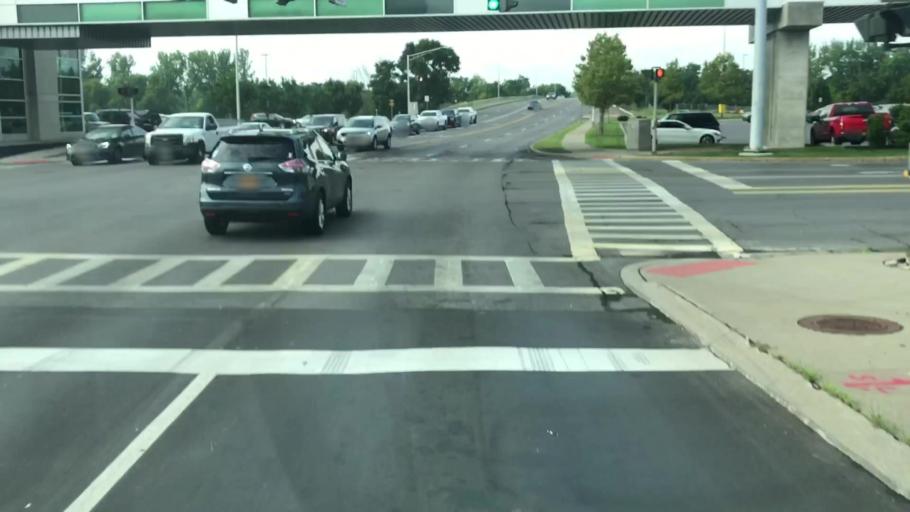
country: US
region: New York
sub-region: Onondaga County
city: Galeville
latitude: 43.0671
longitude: -76.1705
